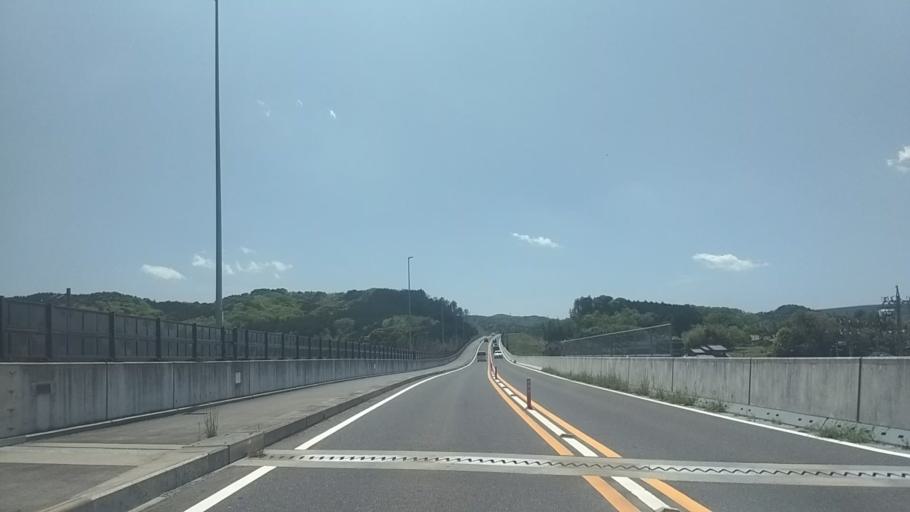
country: JP
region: Aichi
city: Gamagori
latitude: 34.9095
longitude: 137.2763
